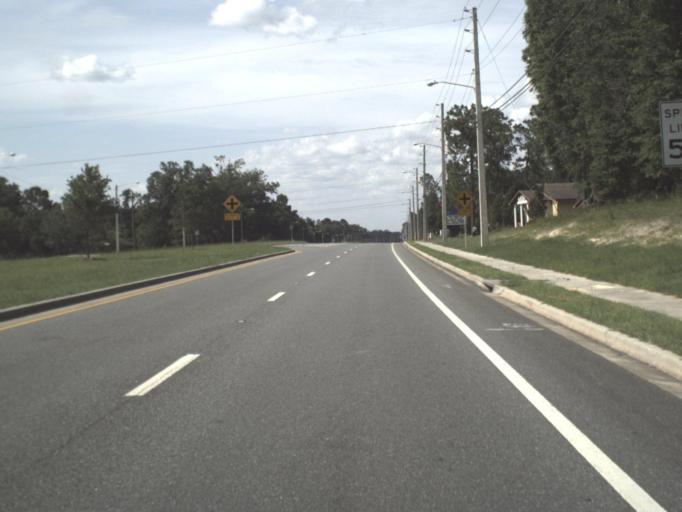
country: US
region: Florida
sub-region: Columbia County
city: Lake City
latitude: 30.1248
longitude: -82.6531
